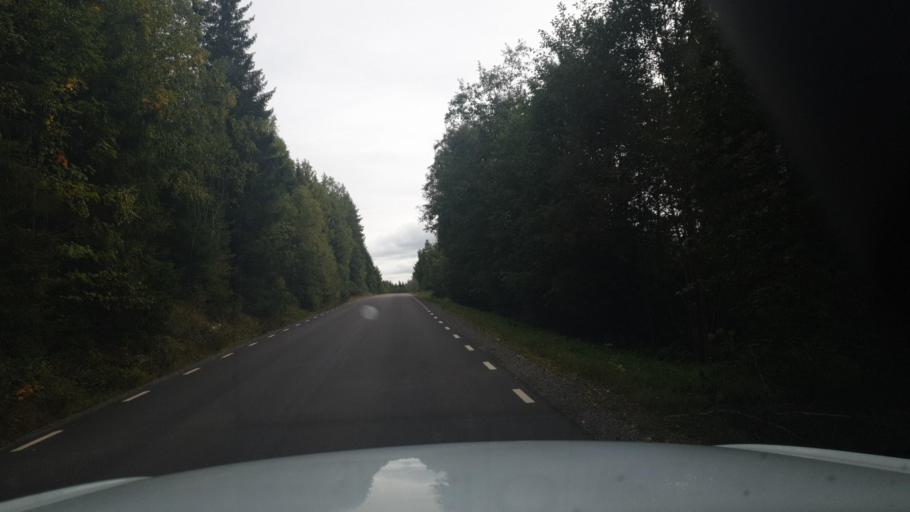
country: SE
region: Vaermland
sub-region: Torsby Kommun
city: Torsby
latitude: 59.9980
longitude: 12.7368
